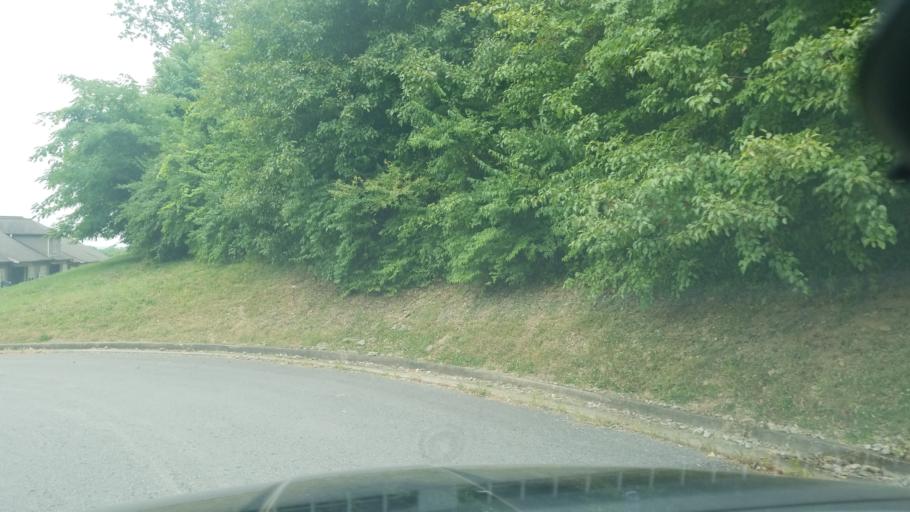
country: US
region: Tennessee
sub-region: Davidson County
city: Goodlettsville
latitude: 36.2556
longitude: -86.7409
